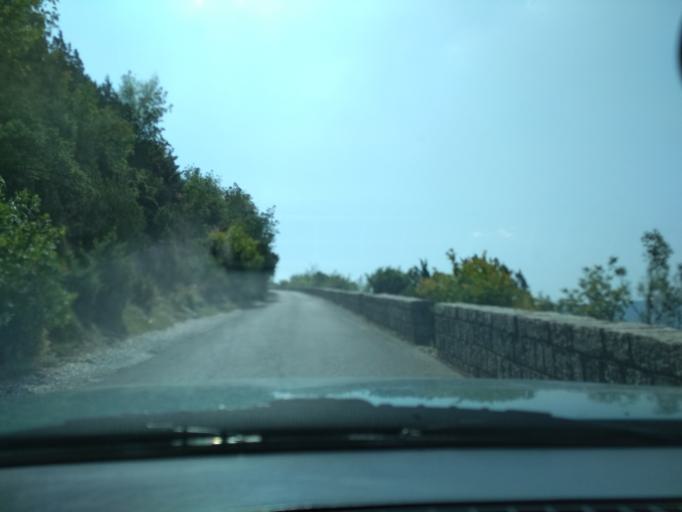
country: ME
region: Kotor
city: Kotor
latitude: 42.3965
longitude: 18.7587
